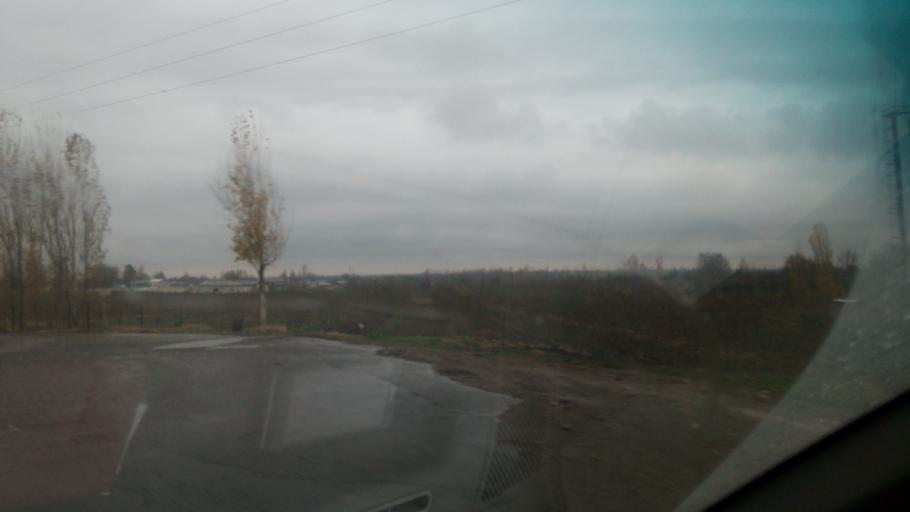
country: UZ
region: Toshkent
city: Urtaowul
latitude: 41.2154
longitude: 69.1285
